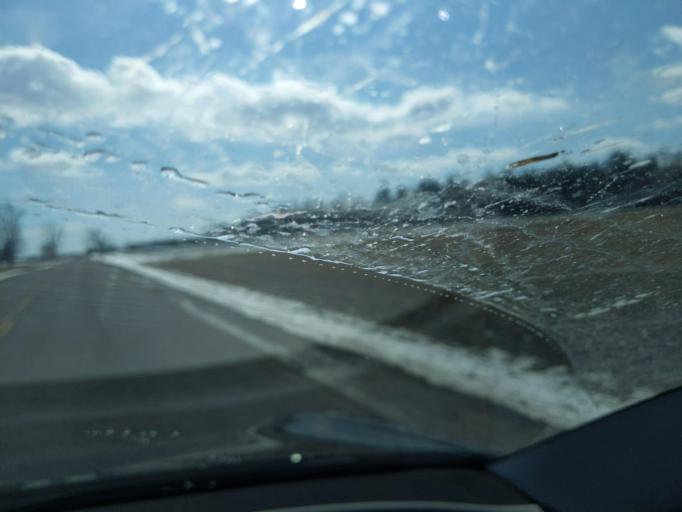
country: US
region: Michigan
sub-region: Livingston County
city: Fowlerville
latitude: 42.5989
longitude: -84.0894
